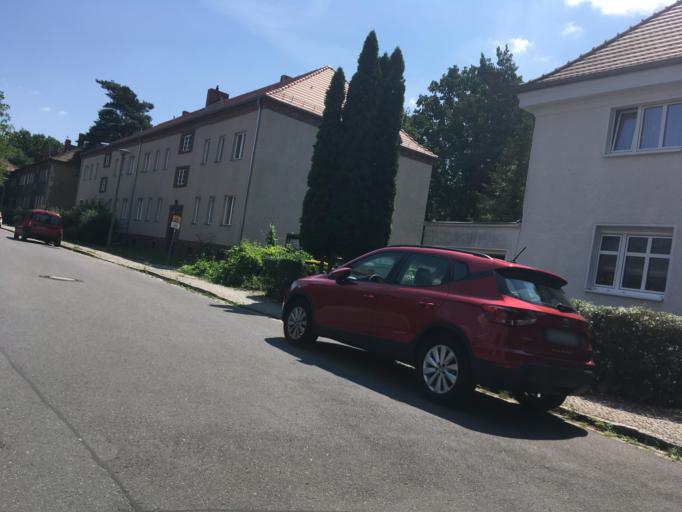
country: DE
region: Berlin
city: Berlin Koepenick
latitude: 52.4601
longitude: 13.5934
